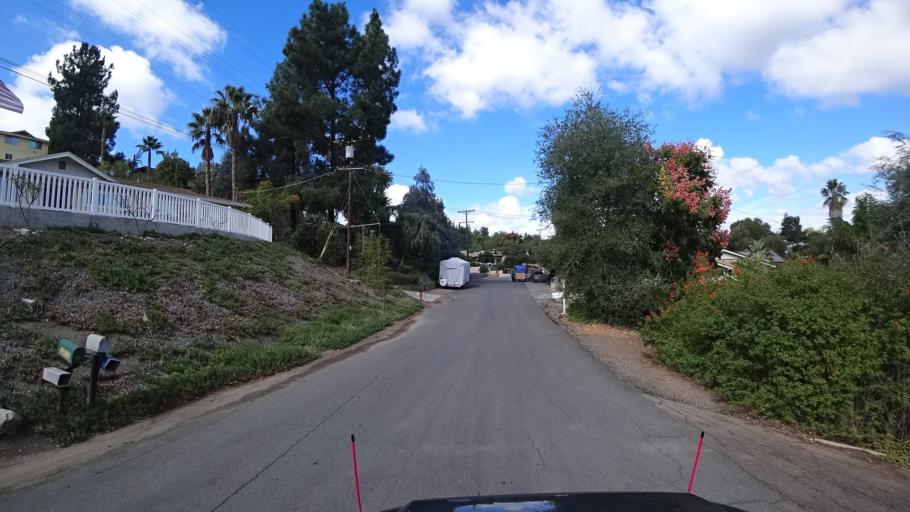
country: US
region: California
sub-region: San Diego County
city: Casa de Oro-Mount Helix
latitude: 32.7368
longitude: -116.9656
